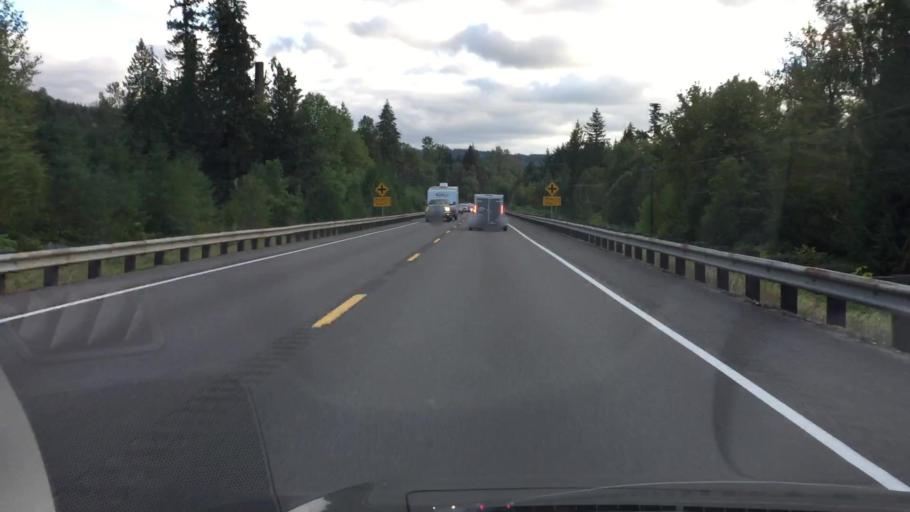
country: US
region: Washington
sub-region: Lewis County
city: Morton
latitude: 46.5247
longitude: -122.5563
